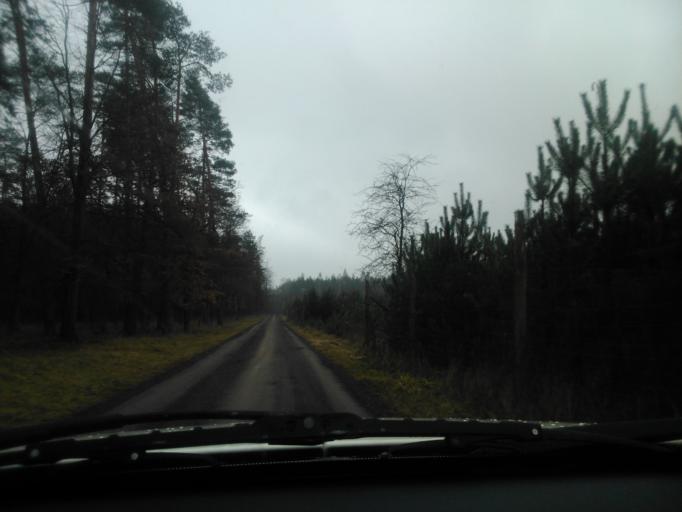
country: PL
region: Kujawsko-Pomorskie
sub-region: Powiat wabrzeski
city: Debowa Laka
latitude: 53.1667
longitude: 19.1371
